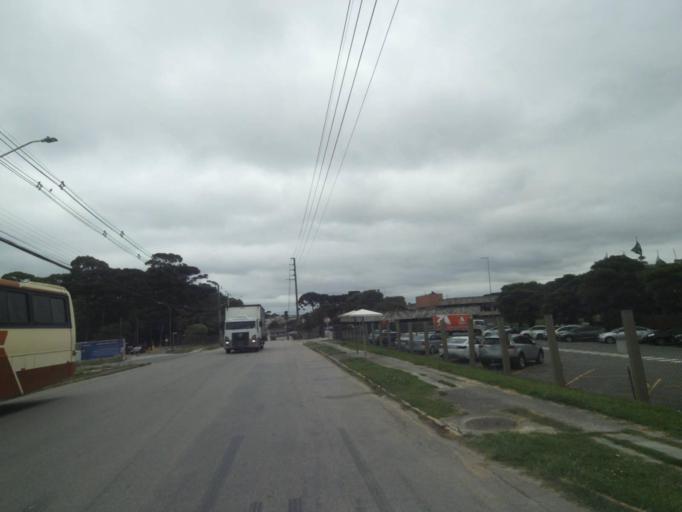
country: BR
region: Parana
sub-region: Sao Jose Dos Pinhais
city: Sao Jose dos Pinhais
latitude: -25.5581
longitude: -49.3100
